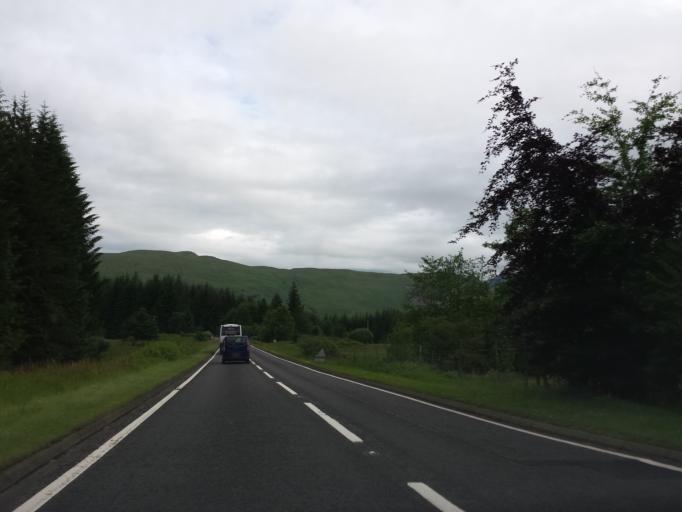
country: GB
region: Scotland
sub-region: Stirling
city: Callander
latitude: 56.4342
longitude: -4.3421
